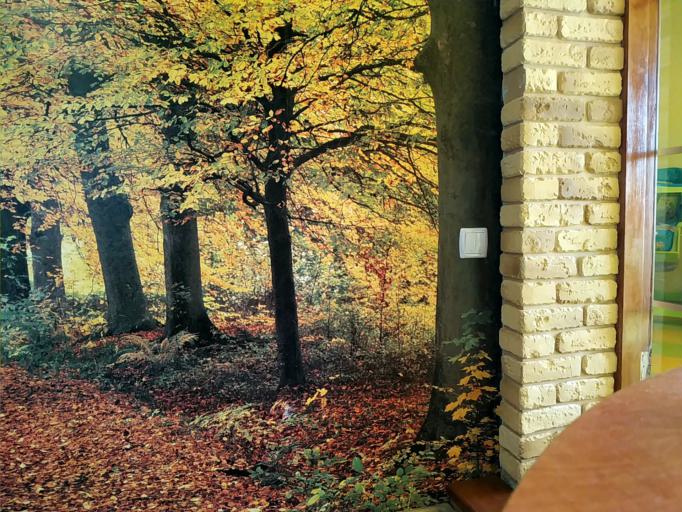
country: RU
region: Novgorod
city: Staraya Russa
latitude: 57.8313
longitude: 31.4897
